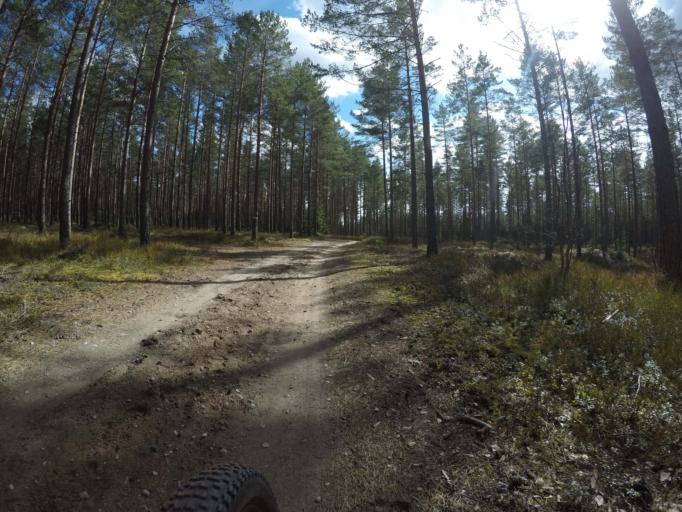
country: SE
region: Vaestmanland
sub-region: Kungsors Kommun
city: Kungsoer
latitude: 59.3609
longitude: 16.1090
